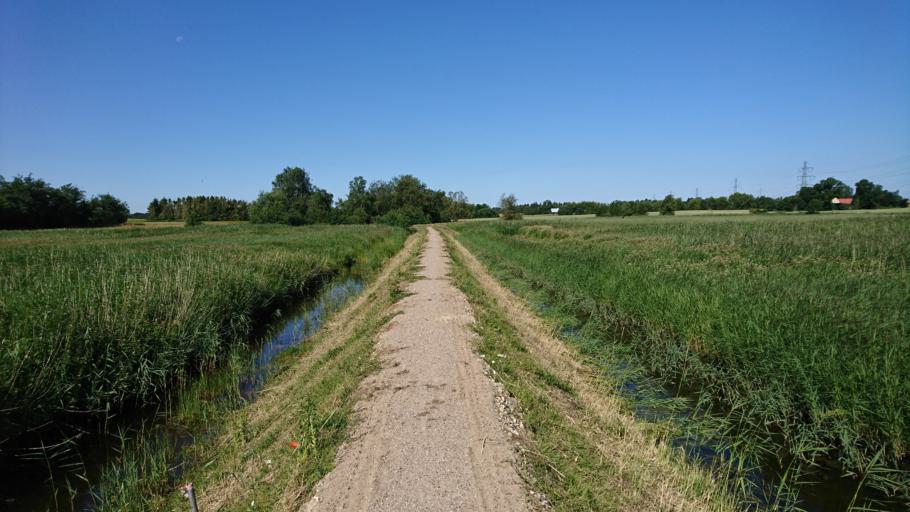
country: DK
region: Capital Region
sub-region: Frederikssund Kommune
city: Frederikssund
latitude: 55.7937
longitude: 12.0456
